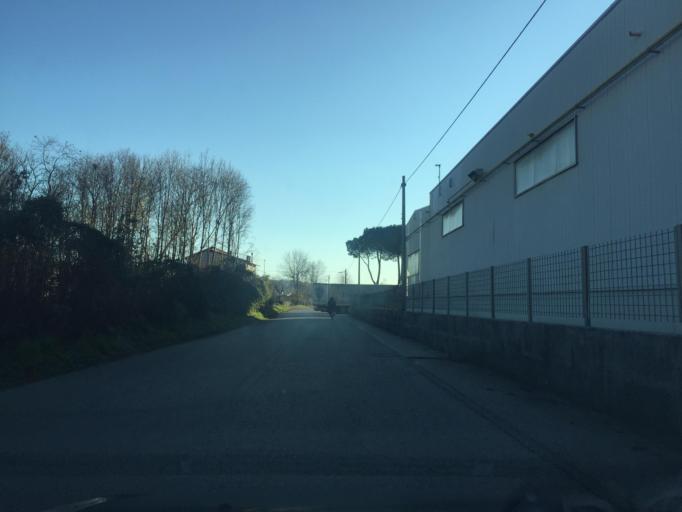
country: IT
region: Friuli Venezia Giulia
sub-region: Provincia di Udine
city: Osoppo
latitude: 46.2502
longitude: 13.1097
